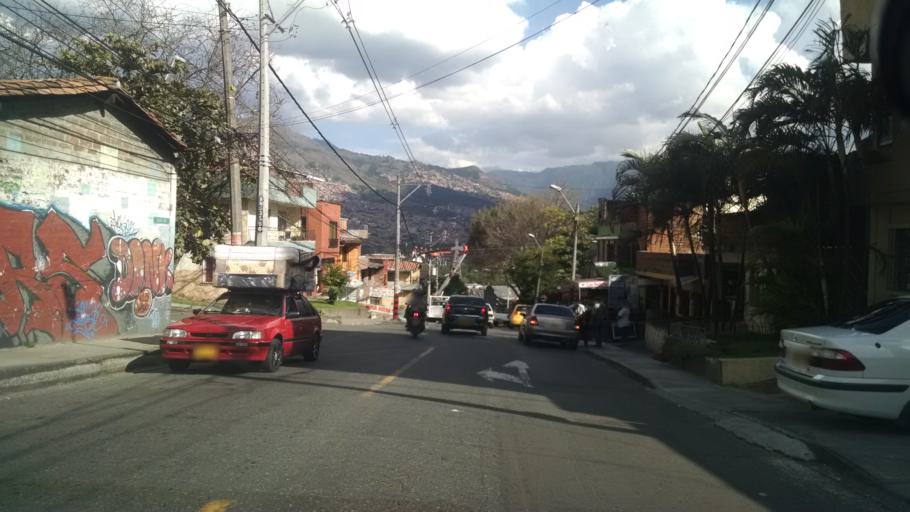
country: CO
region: Antioquia
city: Medellin
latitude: 6.2787
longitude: -75.5770
